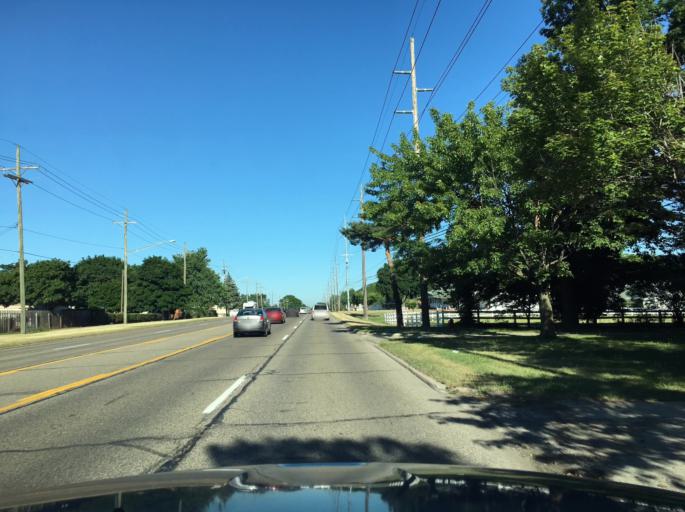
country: US
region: Michigan
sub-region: Macomb County
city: Fraser
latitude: 42.5384
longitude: -82.9740
